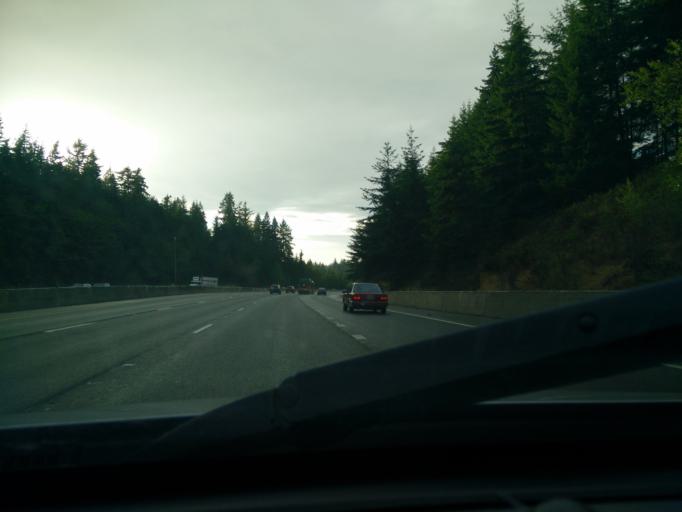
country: US
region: Washington
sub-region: Snohomish County
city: Martha Lake
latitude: 47.8232
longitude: -122.2495
